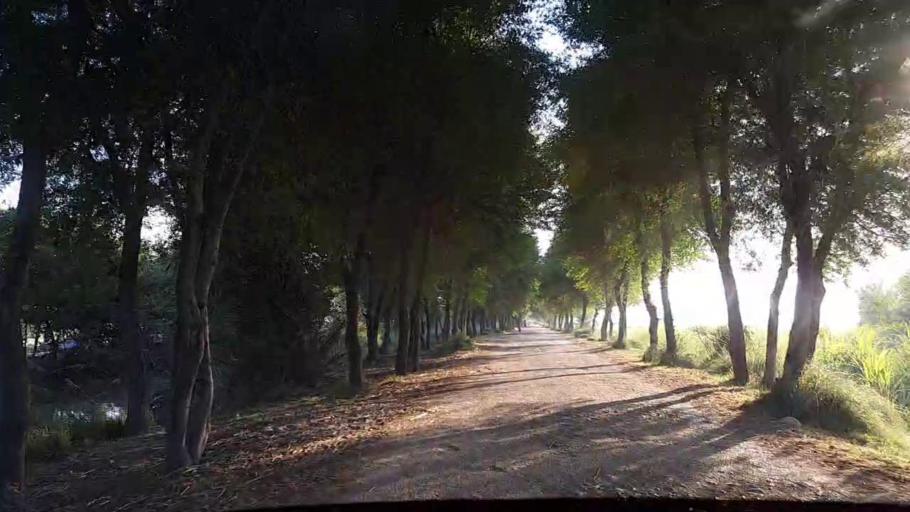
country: PK
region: Sindh
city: Sobhadero
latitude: 27.4106
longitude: 68.3944
